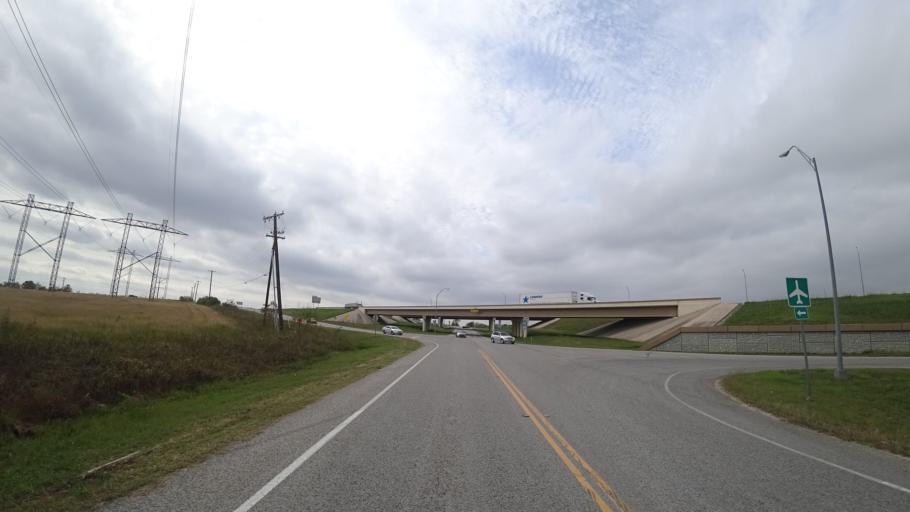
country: US
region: Texas
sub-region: Travis County
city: Pflugerville
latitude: 30.4069
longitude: -97.5825
